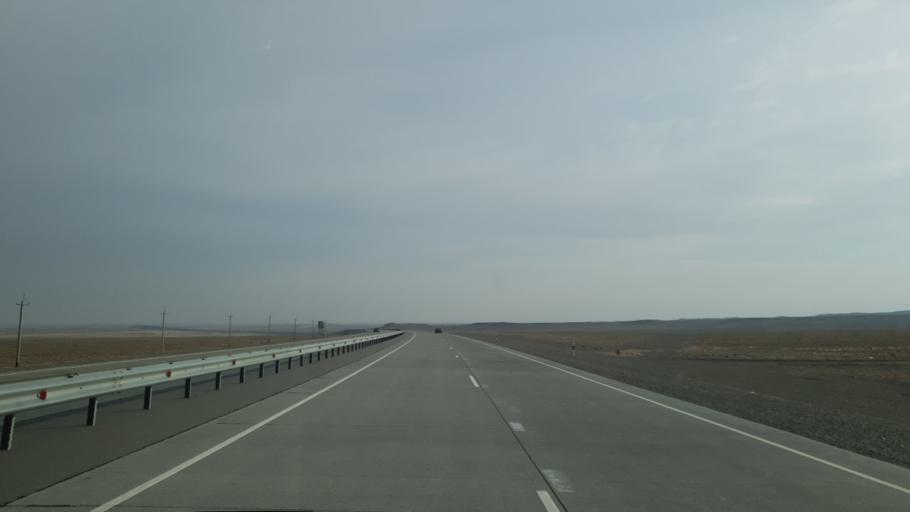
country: KZ
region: Almaty Oblysy
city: Kegen
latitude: 43.7544
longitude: 79.1205
